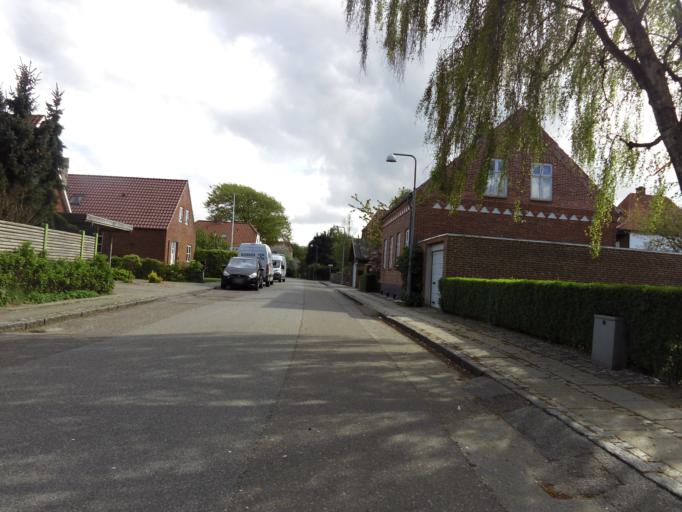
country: DK
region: South Denmark
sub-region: Esbjerg Kommune
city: Ribe
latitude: 55.3295
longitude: 8.7732
